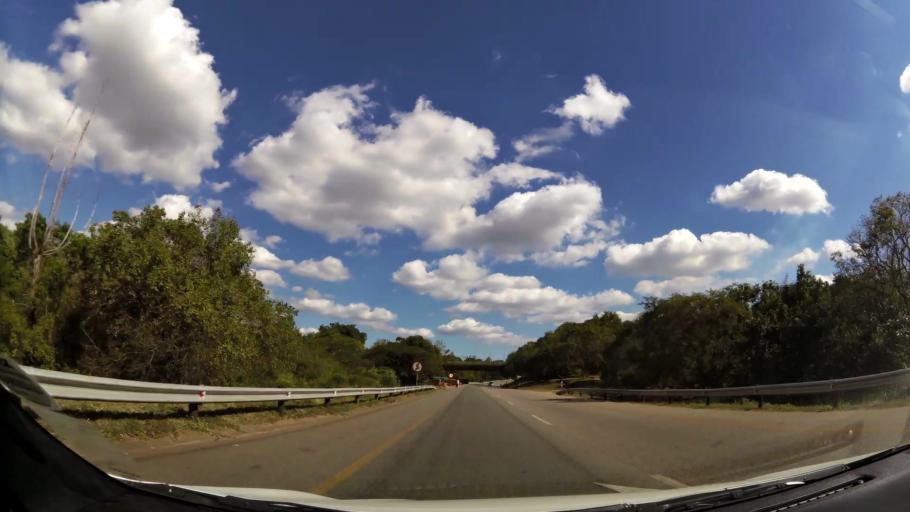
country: ZA
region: Limpopo
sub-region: Mopani District Municipality
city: Tzaneen
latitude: -23.8281
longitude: 30.1522
